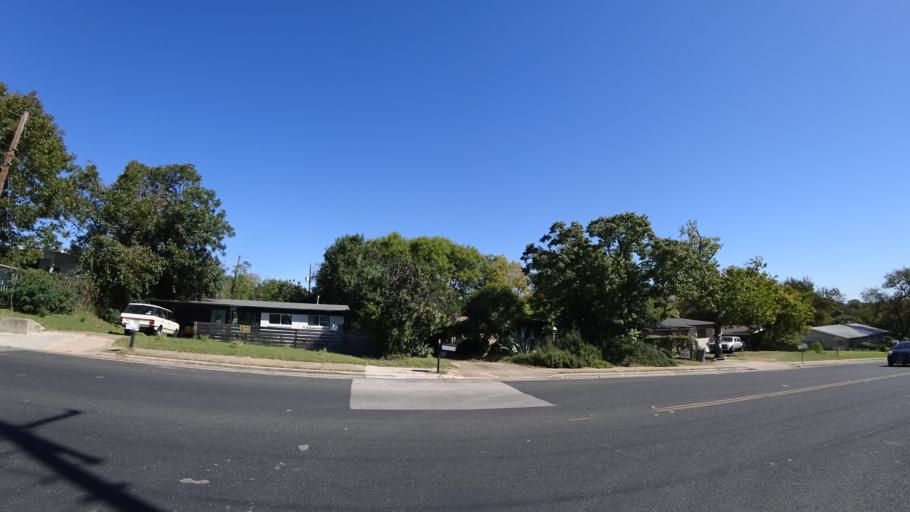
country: US
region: Texas
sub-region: Travis County
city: Austin
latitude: 30.2849
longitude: -97.6806
